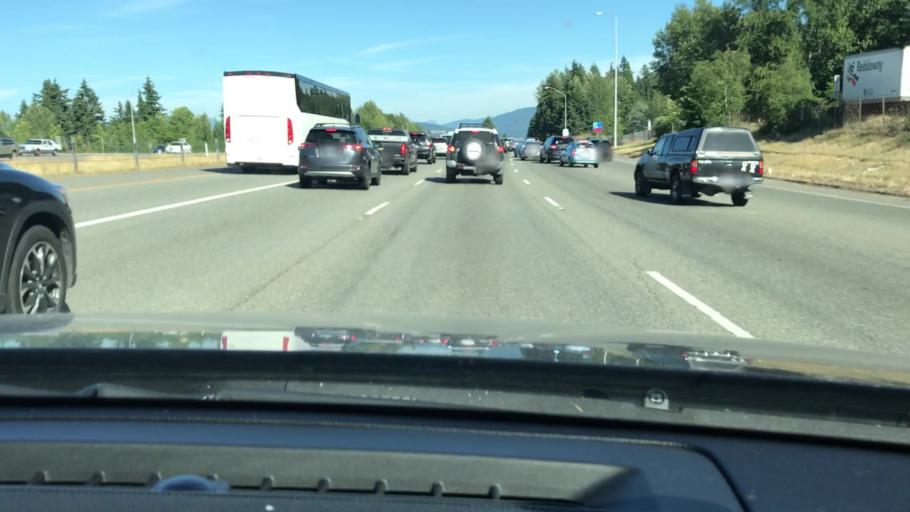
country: US
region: Washington
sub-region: King County
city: Eastgate
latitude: 47.5776
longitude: -122.1317
